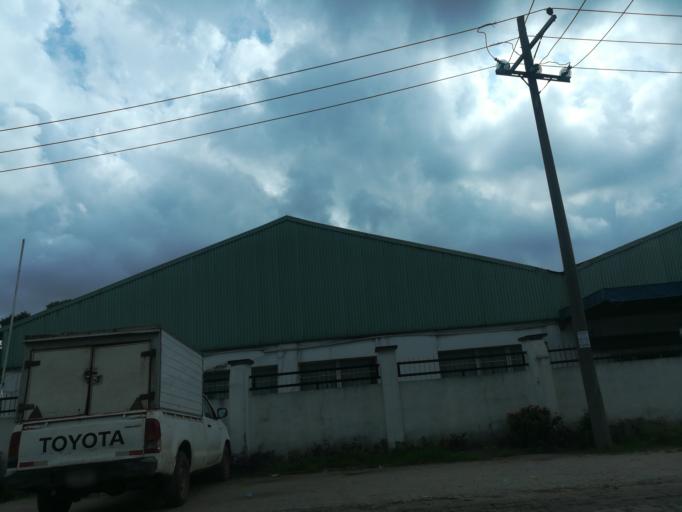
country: NG
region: Lagos
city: Somolu
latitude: 6.5473
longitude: 3.3573
